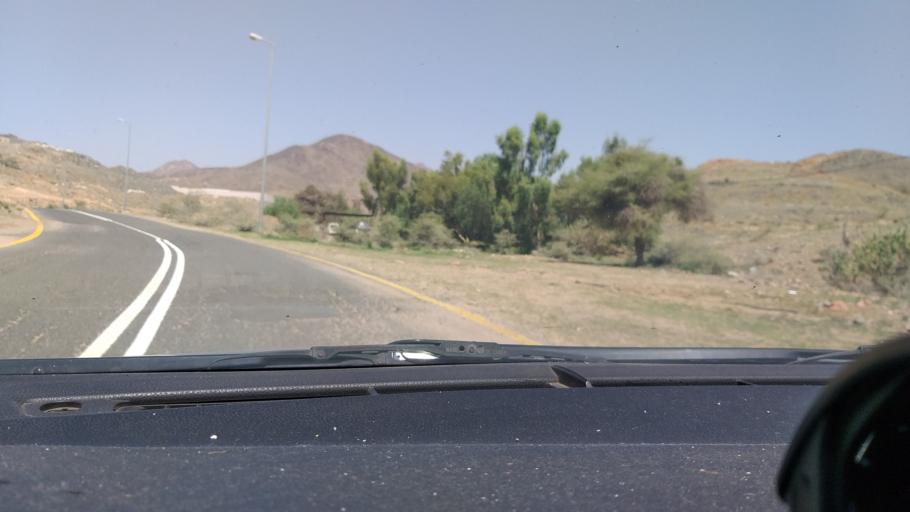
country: SA
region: Makkah
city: Ash Shafa
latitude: 21.1568
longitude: 40.3641
